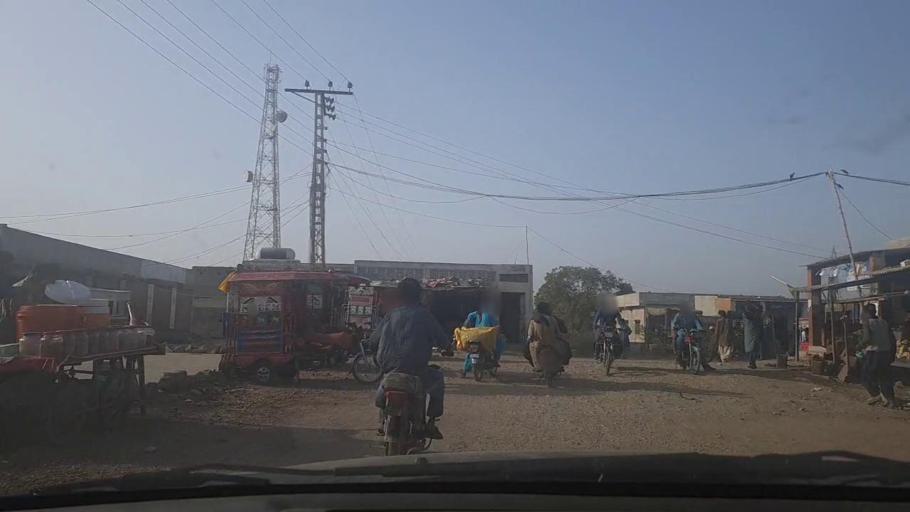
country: PK
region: Sindh
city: Keti Bandar
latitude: 24.3045
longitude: 67.6044
